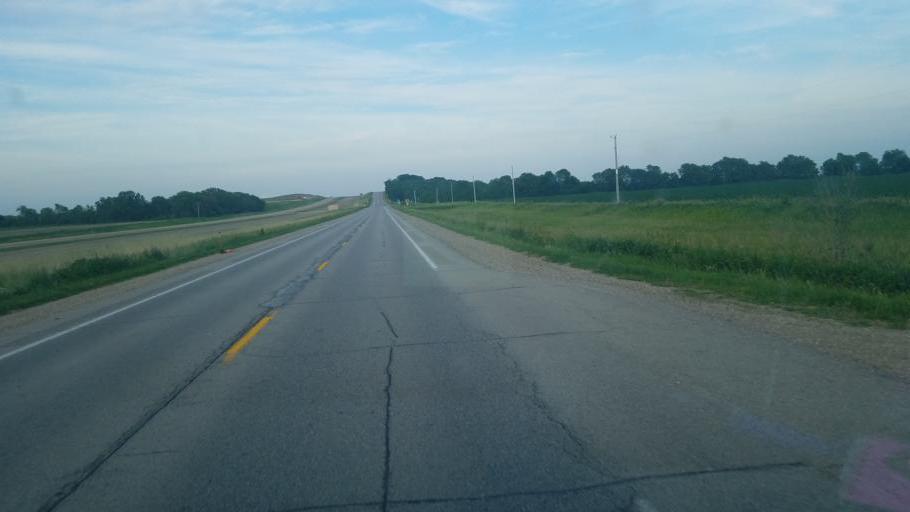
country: US
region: Iowa
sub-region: Tama County
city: Tama
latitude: 41.9639
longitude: -92.4641
